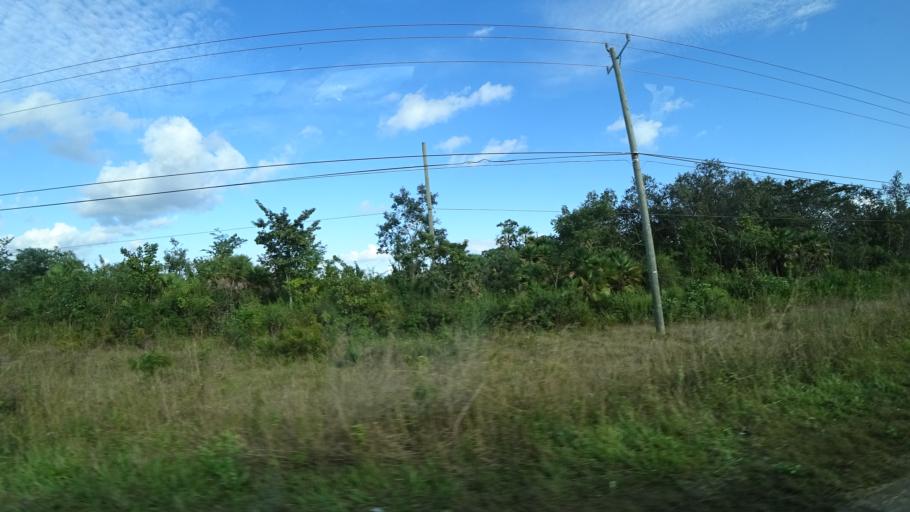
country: BZ
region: Belize
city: Belize City
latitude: 17.5735
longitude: -88.3847
